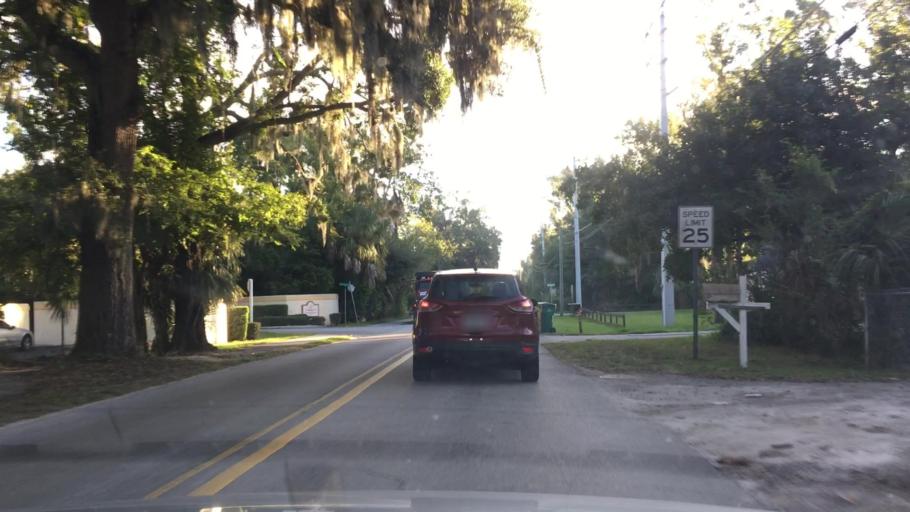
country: US
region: Florida
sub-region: Volusia County
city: Holly Hill
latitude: 29.2478
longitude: -81.0657
